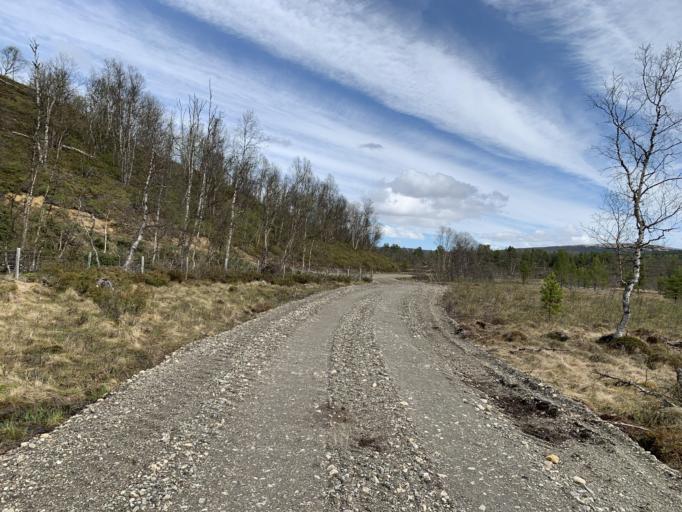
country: NO
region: Hedmark
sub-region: Alvdal
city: Alvdal
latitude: 62.4129
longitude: 10.4030
